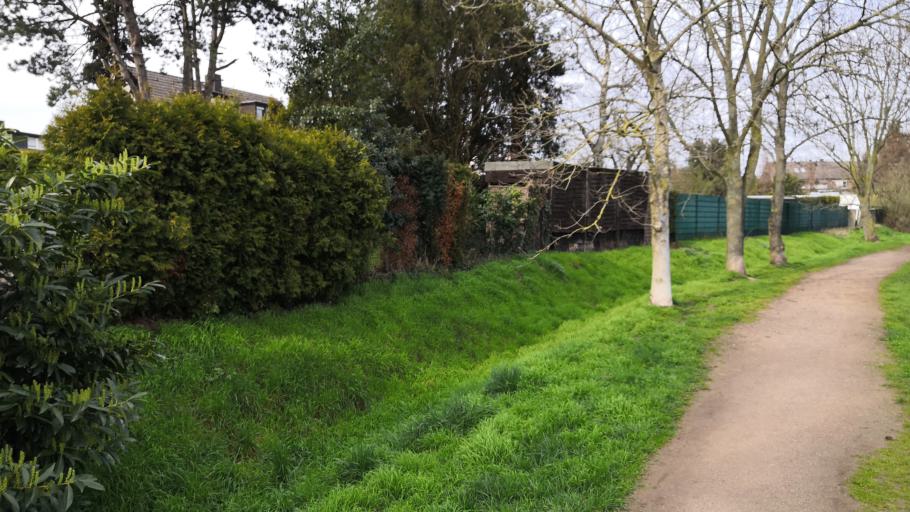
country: DE
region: North Rhine-Westphalia
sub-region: Regierungsbezirk Dusseldorf
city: Moers
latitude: 51.3900
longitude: 6.6507
